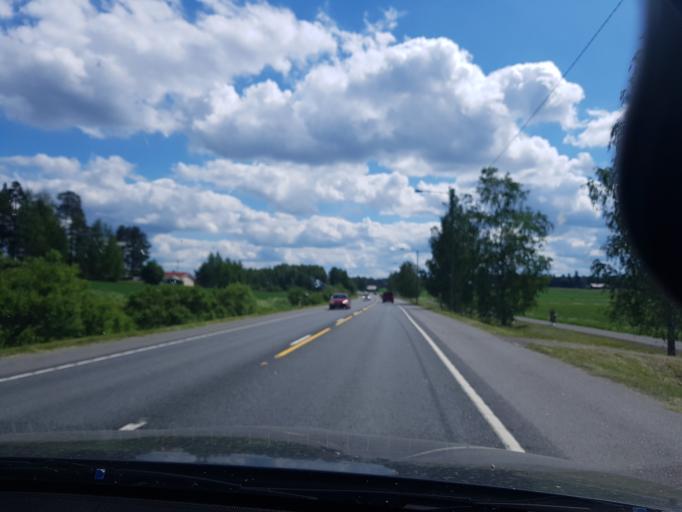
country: FI
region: Haeme
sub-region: Haemeenlinna
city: Parola
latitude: 61.0466
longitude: 24.3971
